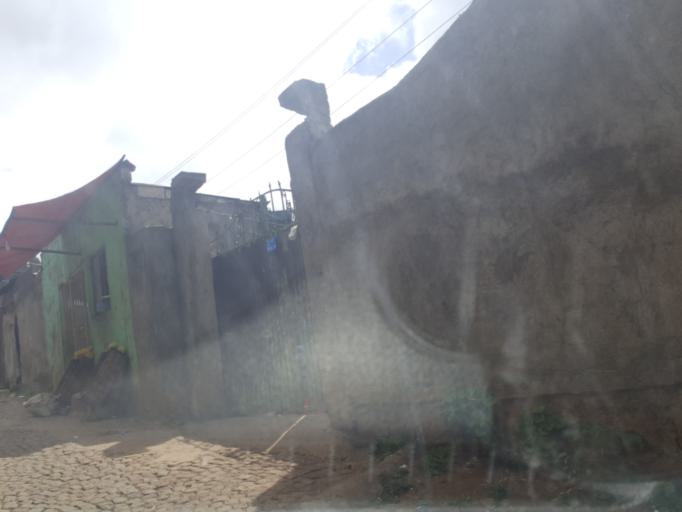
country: ET
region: Adis Abeba
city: Addis Ababa
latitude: 9.0682
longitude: 38.7383
